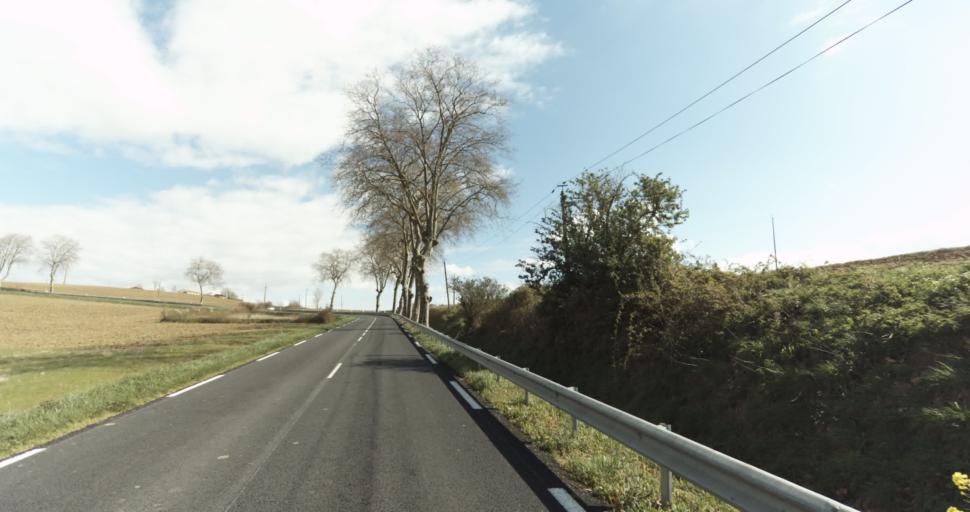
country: FR
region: Midi-Pyrenees
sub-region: Departement de la Haute-Garonne
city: Auterive
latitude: 43.3578
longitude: 1.4931
